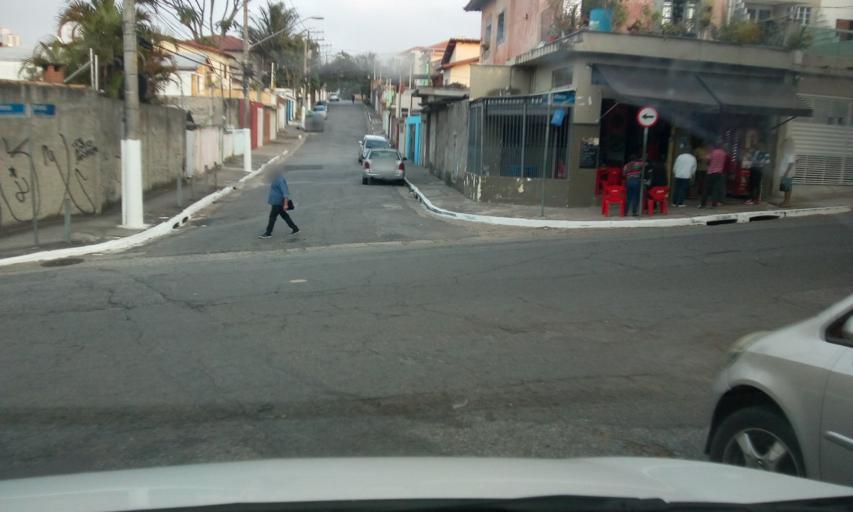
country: BR
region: Sao Paulo
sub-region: Sao Paulo
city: Sao Paulo
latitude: -23.6170
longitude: -46.6452
